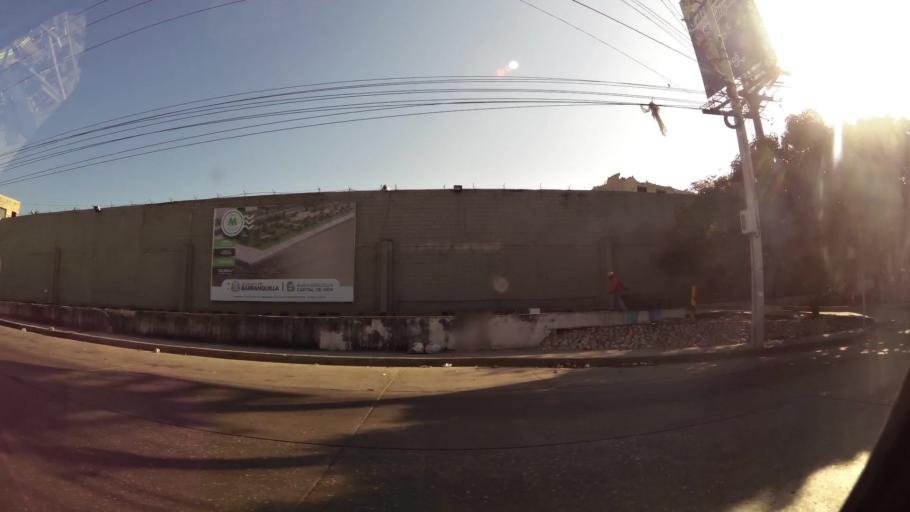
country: CO
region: Atlantico
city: Barranquilla
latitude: 11.0143
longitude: -74.7941
